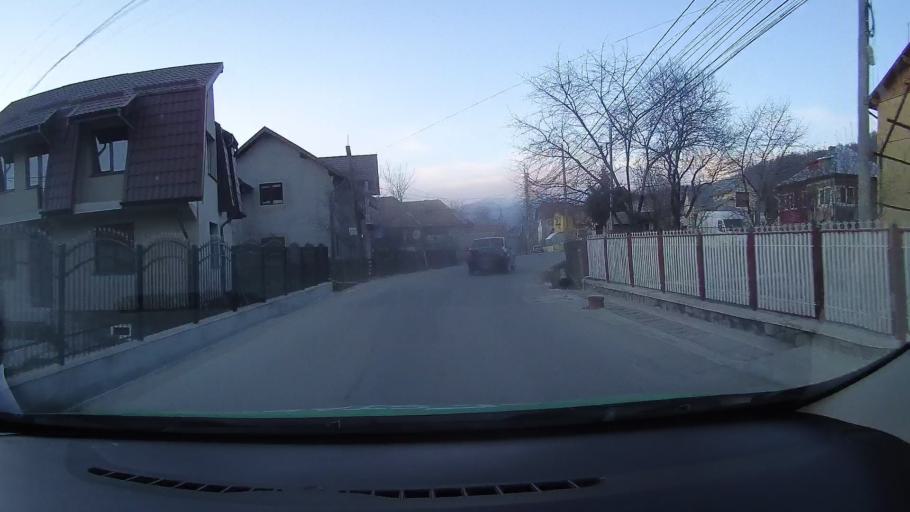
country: RO
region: Prahova
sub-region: Comuna Comarnic
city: Comarnic
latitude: 45.2484
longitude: 25.6369
